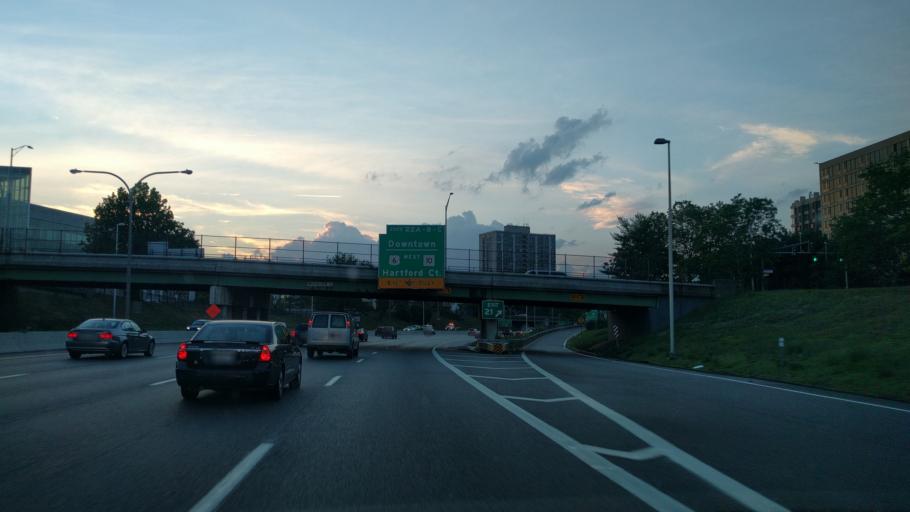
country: US
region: Rhode Island
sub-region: Providence County
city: Providence
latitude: 41.8194
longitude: -71.4187
